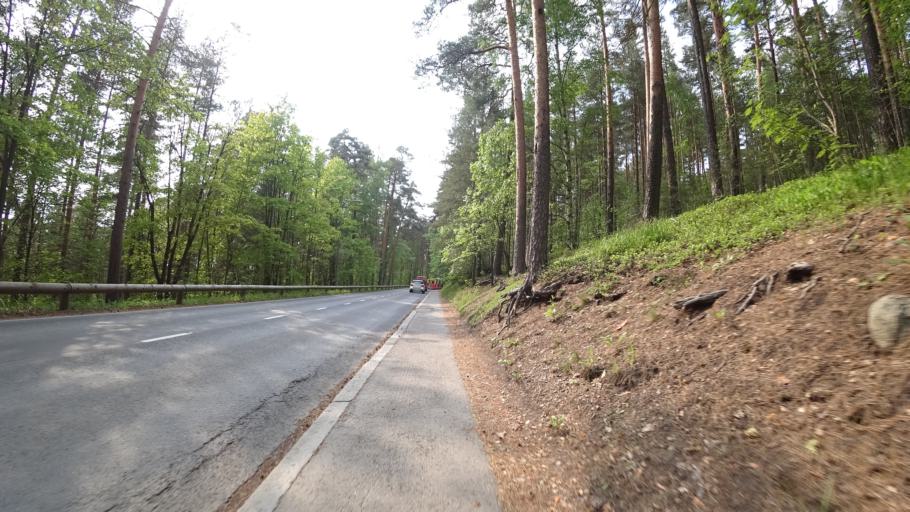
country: FI
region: Pirkanmaa
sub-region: Tampere
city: Tampere
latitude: 61.4933
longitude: 23.7387
